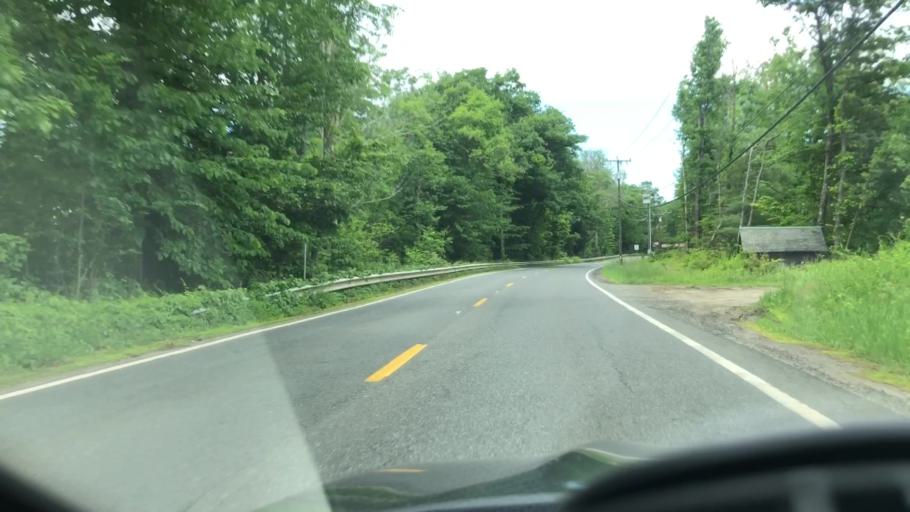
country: US
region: Massachusetts
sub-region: Hampshire County
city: Westhampton
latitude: 42.2525
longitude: -72.8673
